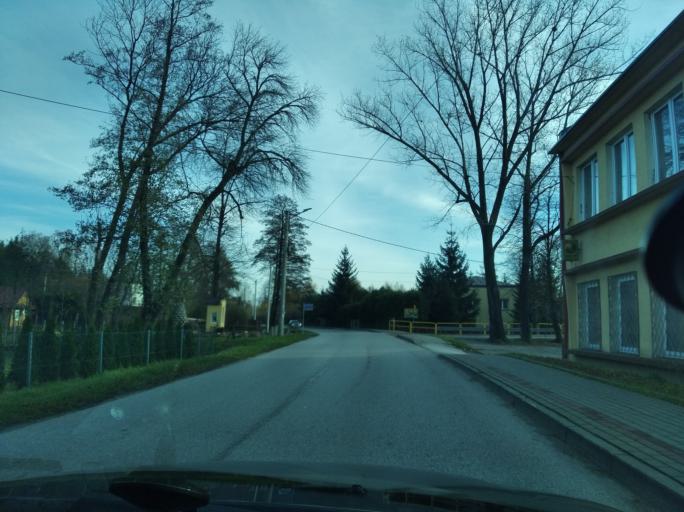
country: PL
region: Subcarpathian Voivodeship
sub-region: Powiat lancucki
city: Kraczkowa
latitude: 50.0379
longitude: 22.1688
